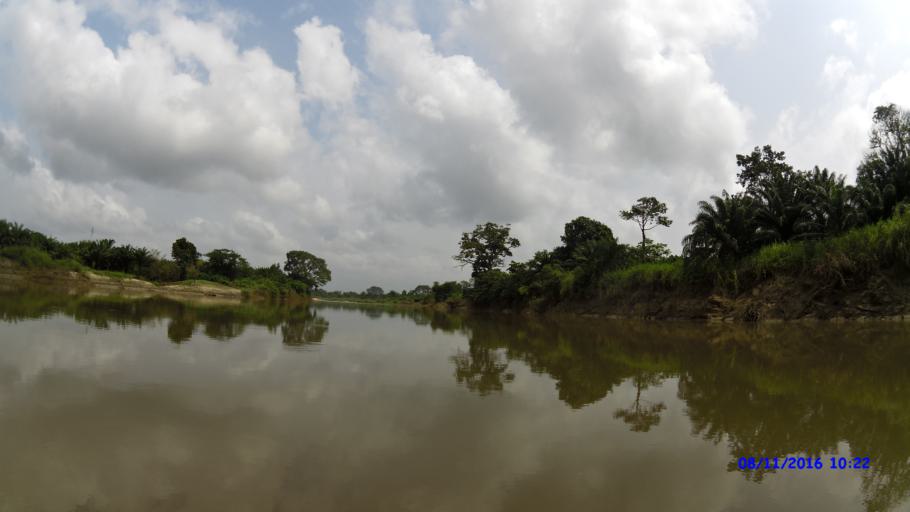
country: BJ
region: Mono
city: Come
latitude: 6.4633
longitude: 1.7461
